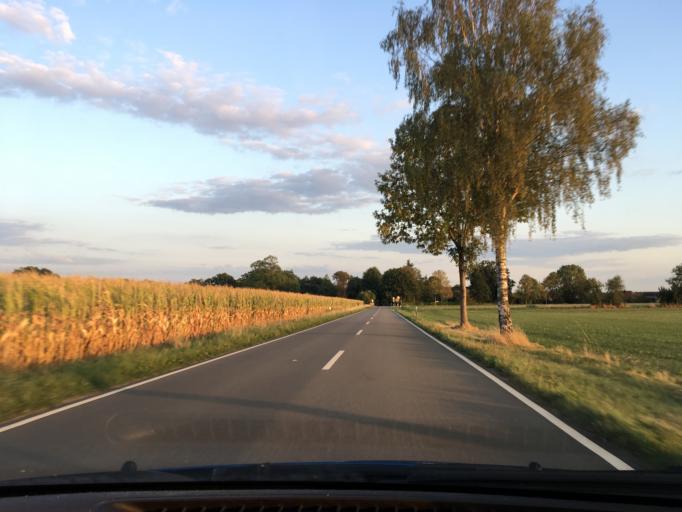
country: DE
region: Lower Saxony
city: Tosterglope
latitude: 53.2132
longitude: 10.8172
